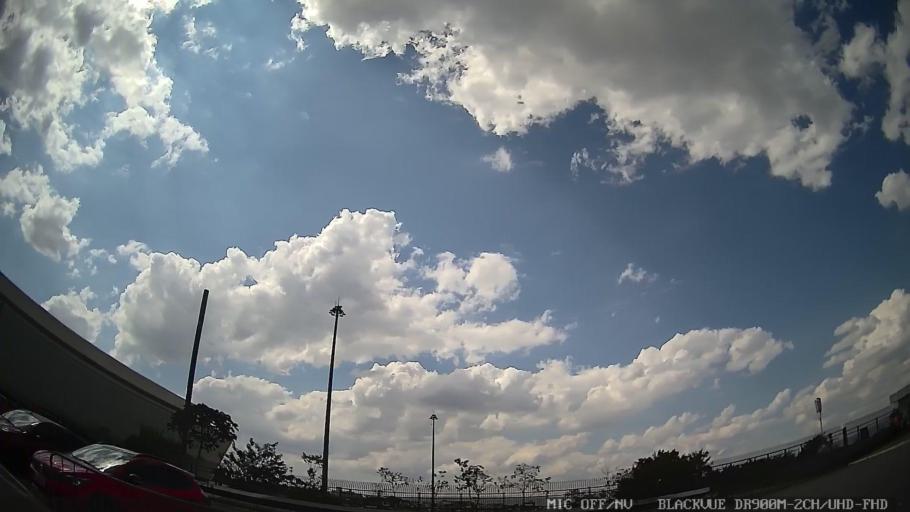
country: BR
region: Sao Paulo
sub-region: Ferraz De Vasconcelos
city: Ferraz de Vasconcelos
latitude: -23.5460
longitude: -46.4716
